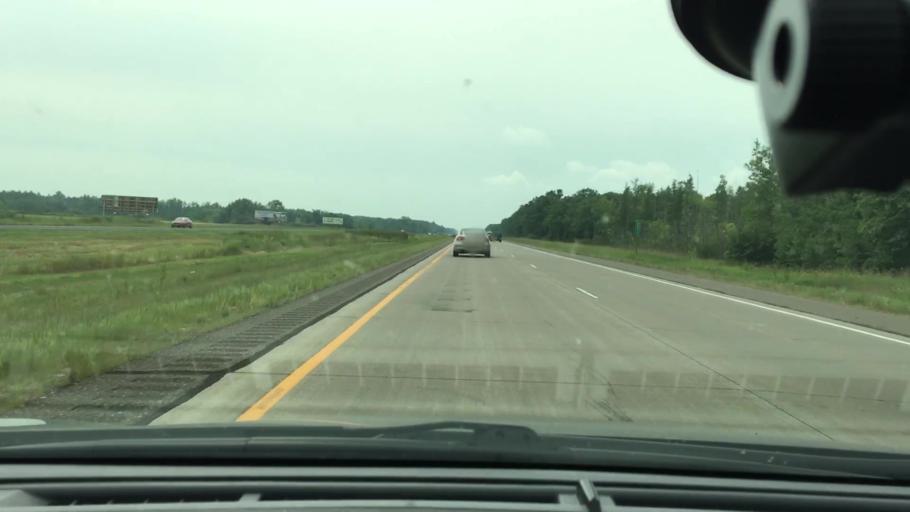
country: US
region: Minnesota
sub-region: Mille Lacs County
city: Vineland
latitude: 46.0339
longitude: -93.6630
